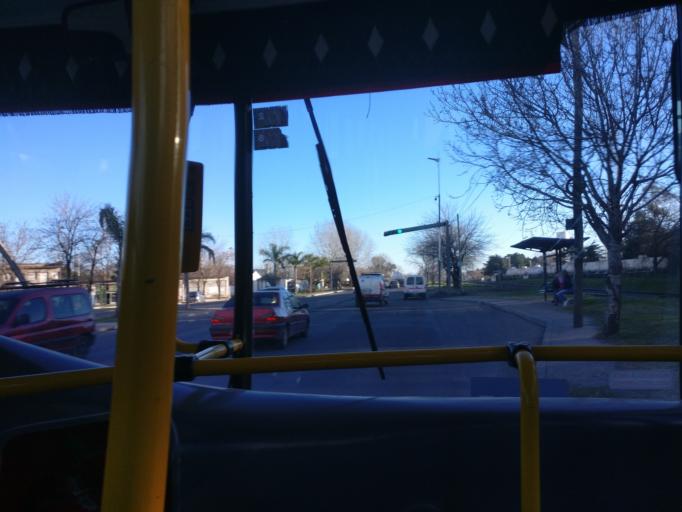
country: AR
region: Buenos Aires
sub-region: Partido de Ezeiza
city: Ezeiza
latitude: -34.9009
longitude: -58.5824
